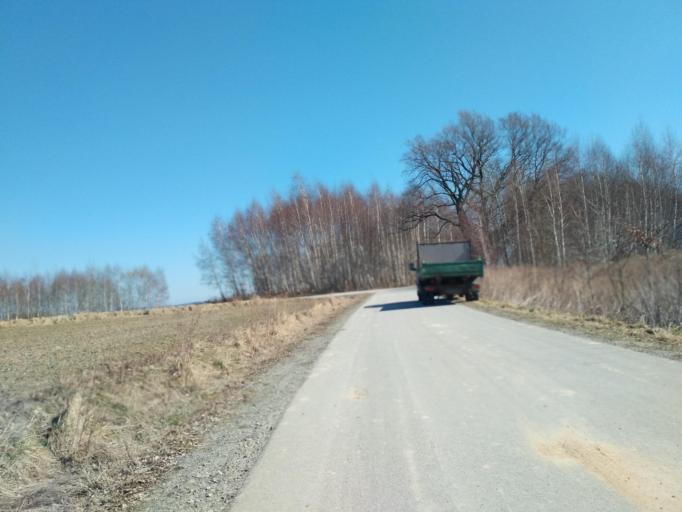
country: PL
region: Subcarpathian Voivodeship
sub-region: Powiat ropczycko-sedziszowski
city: Niedzwiada
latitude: 49.9557
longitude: 21.5521
